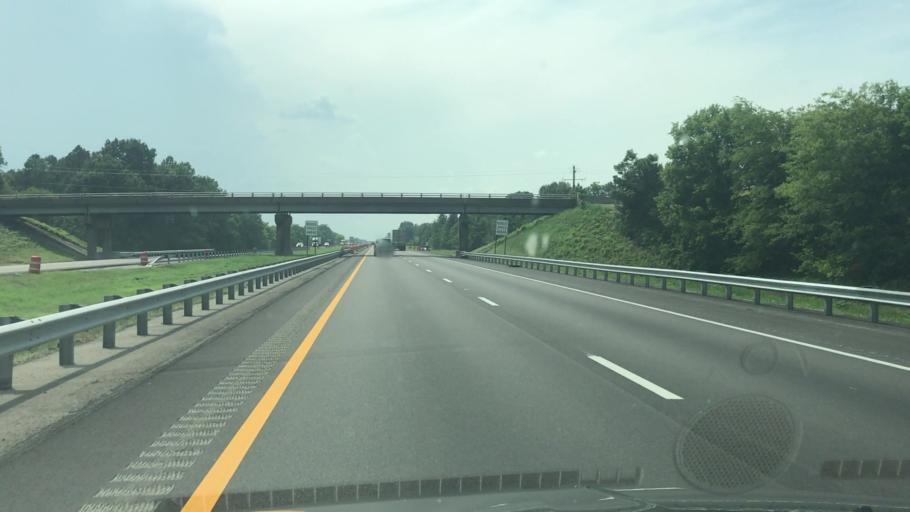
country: US
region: Arkansas
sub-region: Crittenden County
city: Earle
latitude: 35.1342
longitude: -90.4435
